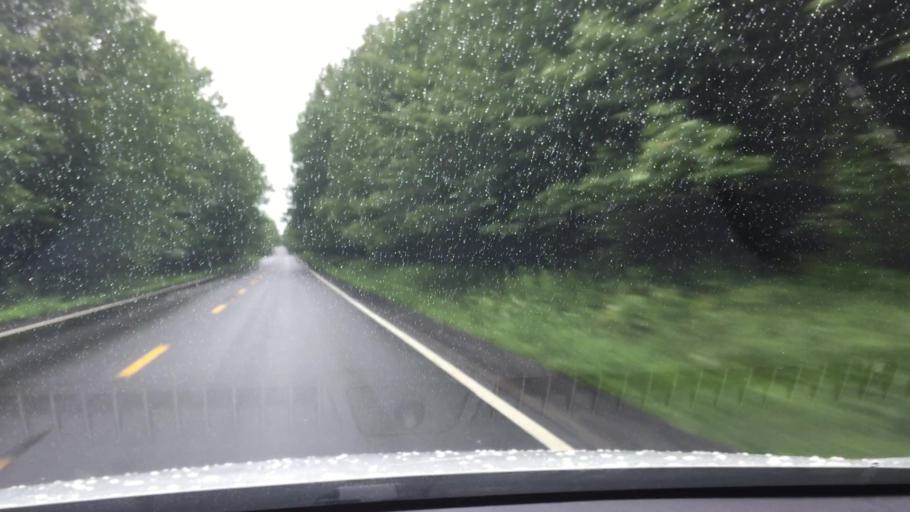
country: US
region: Massachusetts
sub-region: Berkshire County
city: Hinsdale
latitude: 42.3811
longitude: -73.1543
